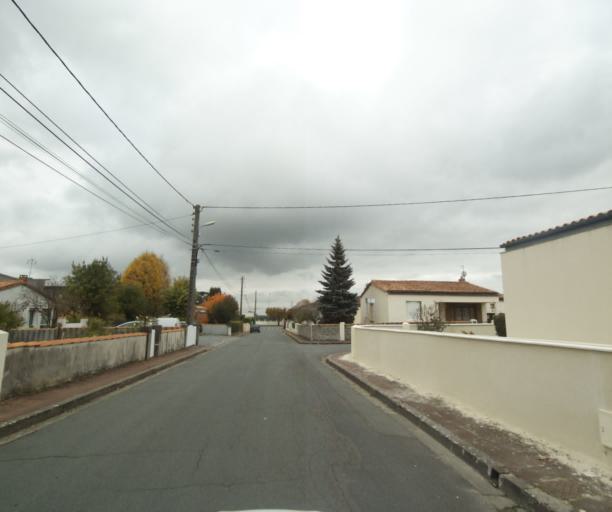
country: FR
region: Poitou-Charentes
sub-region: Departement de la Charente-Maritime
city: Saintes
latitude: 45.7359
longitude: -0.6462
